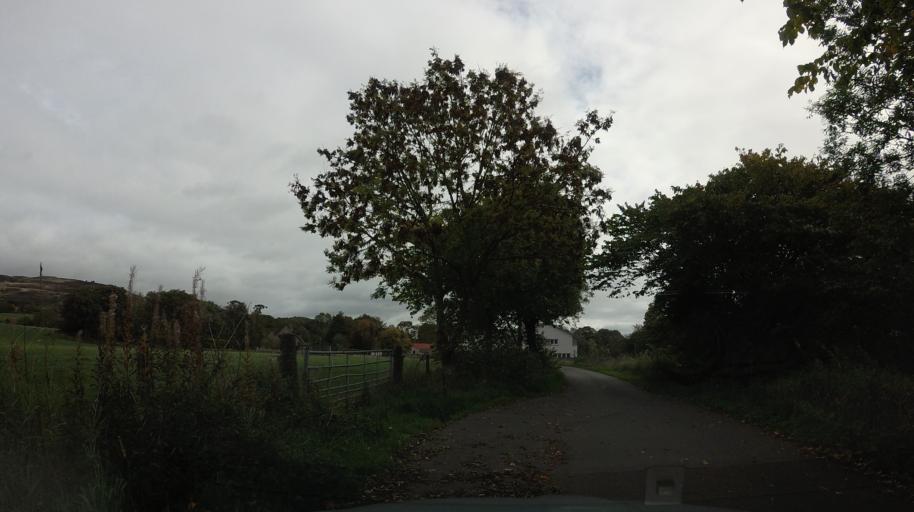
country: GB
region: Scotland
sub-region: Fife
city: Kelty
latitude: 56.1474
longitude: -3.3762
